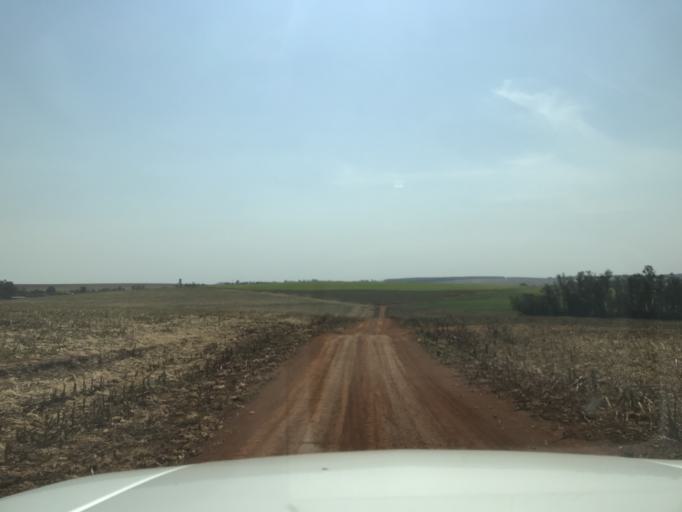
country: BR
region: Parana
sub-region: Palotina
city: Palotina
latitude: -24.2335
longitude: -53.7474
